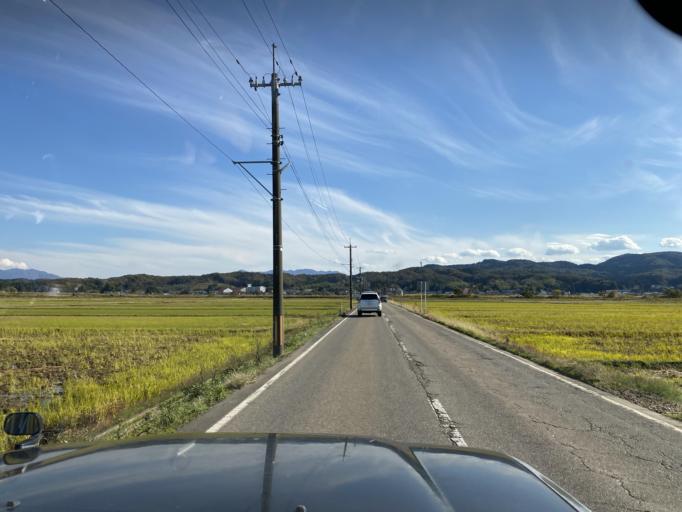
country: JP
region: Niigata
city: Niitsu-honcho
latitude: 37.7582
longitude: 139.0876
